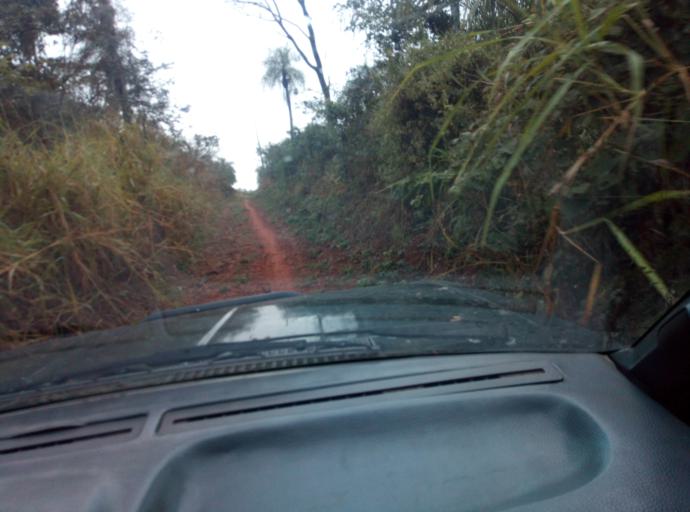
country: PY
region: Caaguazu
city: Carayao
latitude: -25.1938
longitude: -56.3544
